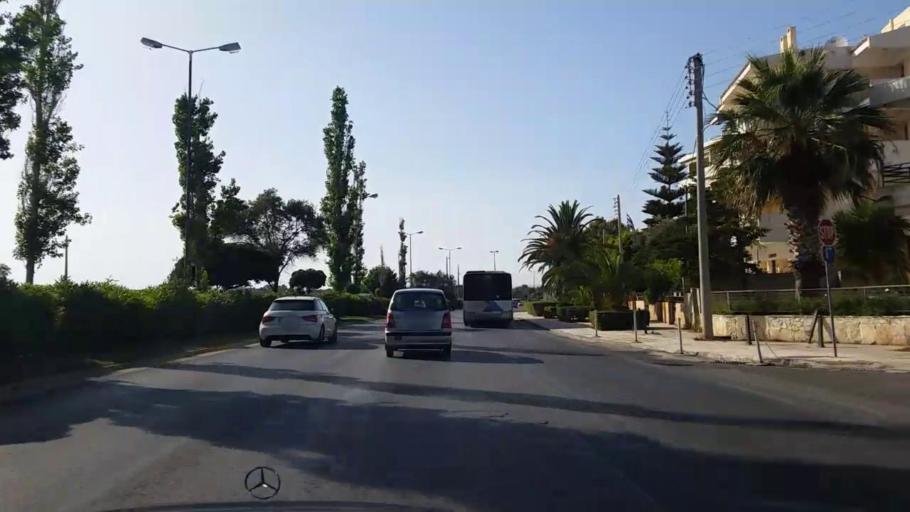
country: GR
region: Attica
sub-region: Nomarchia Athinas
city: Glyfada
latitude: 37.8459
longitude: 23.7546
